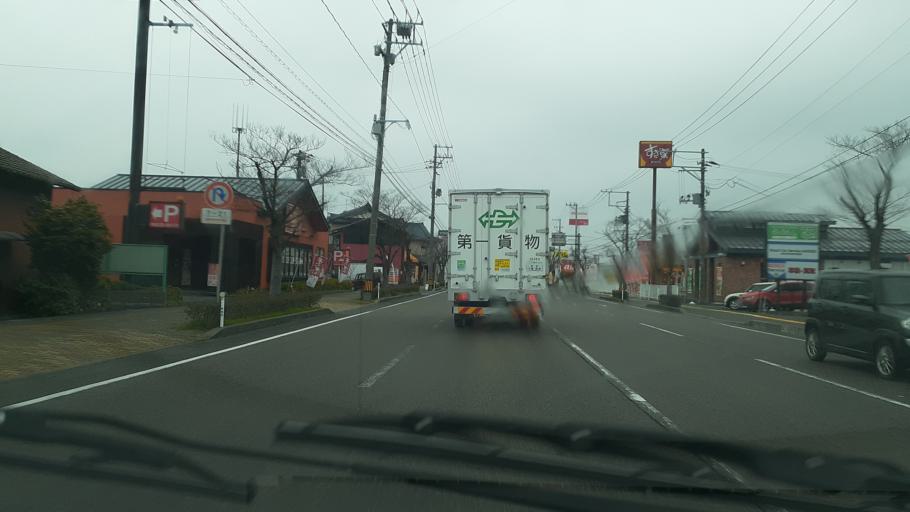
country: JP
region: Niigata
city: Kameda-honcho
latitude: 37.8703
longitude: 139.0900
